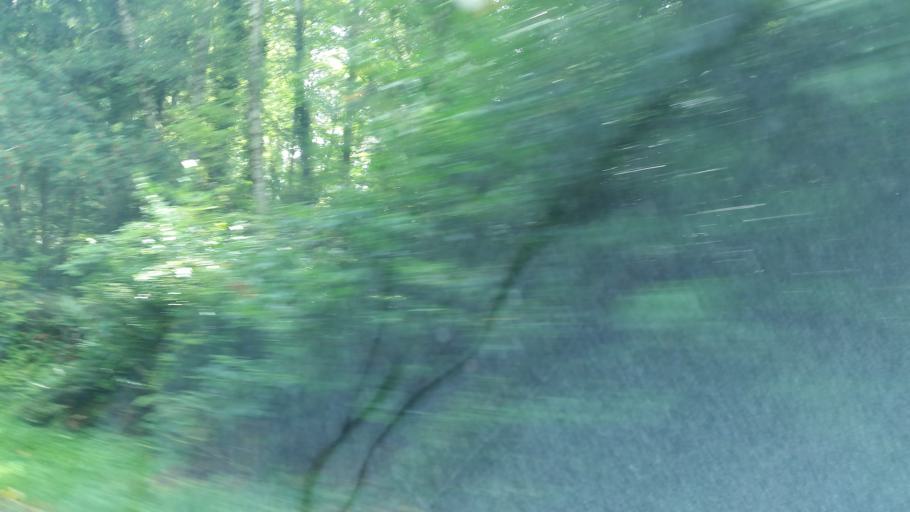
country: US
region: Oregon
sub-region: Clatsop County
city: Astoria
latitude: 46.1863
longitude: -123.8122
